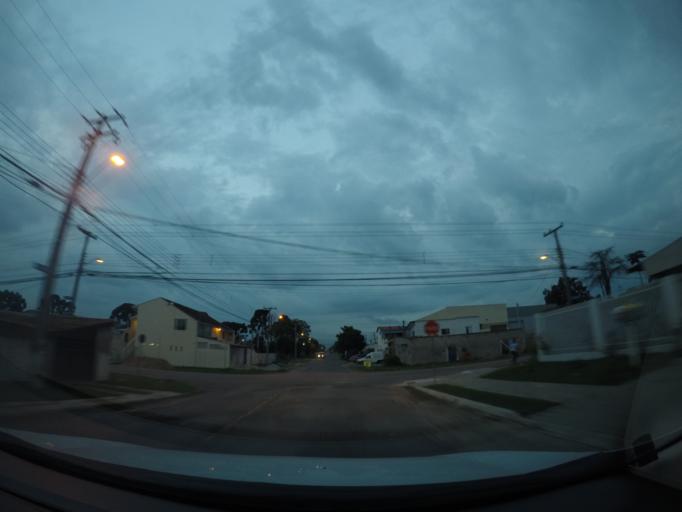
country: BR
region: Parana
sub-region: Sao Jose Dos Pinhais
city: Sao Jose dos Pinhais
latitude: -25.4974
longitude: -49.2341
